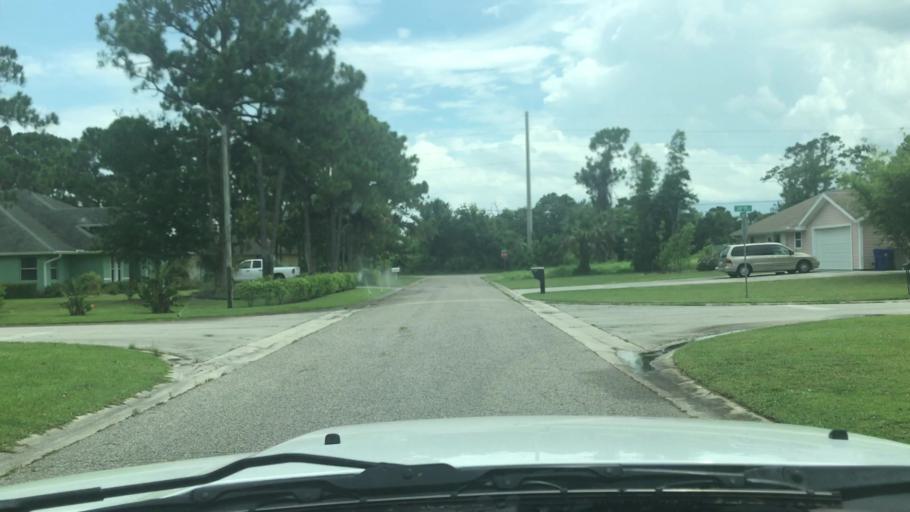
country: US
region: Florida
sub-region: Indian River County
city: Florida Ridge
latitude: 27.5590
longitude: -80.3856
